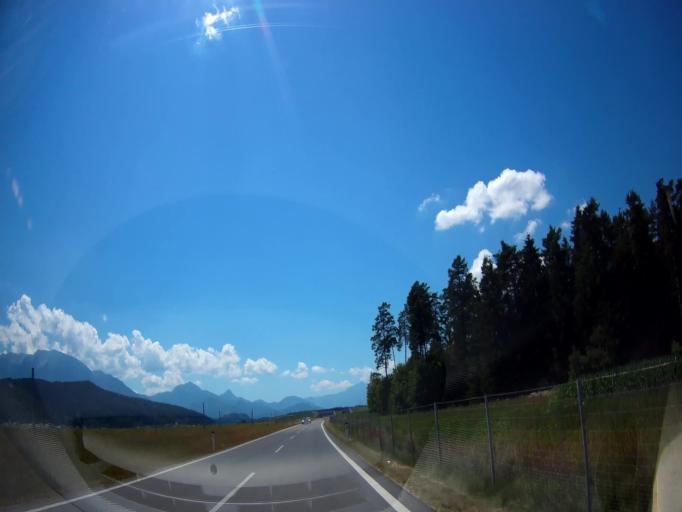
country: AT
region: Carinthia
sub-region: Politischer Bezirk Volkermarkt
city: Bleiburg/Pliberk
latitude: 46.6085
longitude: 14.7800
